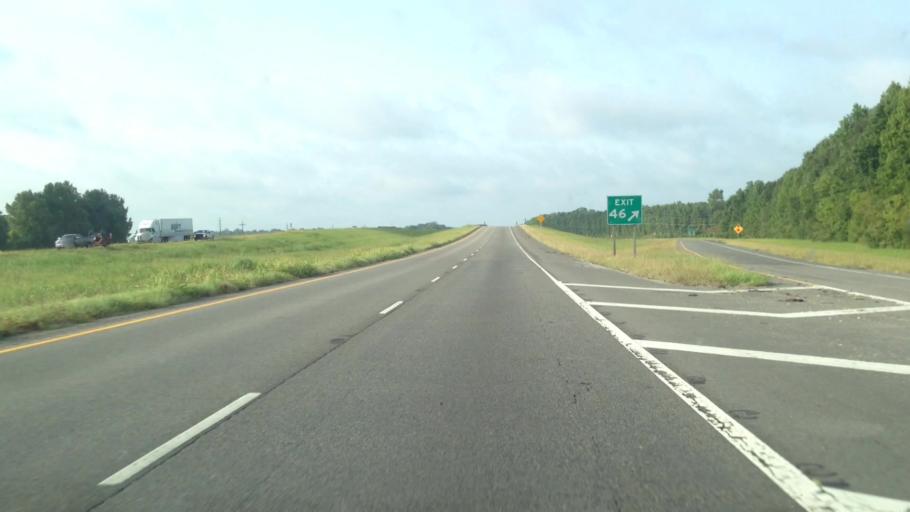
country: US
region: Louisiana
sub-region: Avoyelles Parish
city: Bunkie
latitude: 30.8700
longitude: -92.2281
